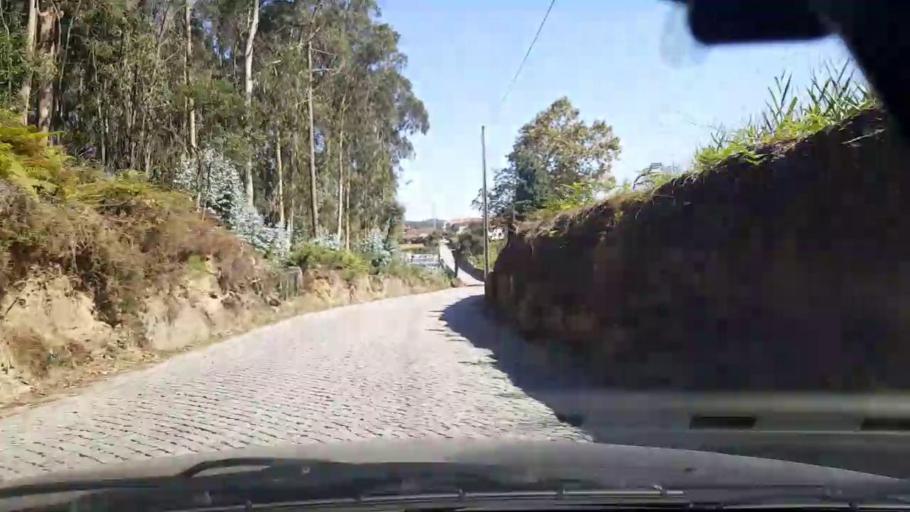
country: PT
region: Porto
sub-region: Vila do Conde
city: Arvore
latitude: 41.3115
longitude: -8.6836
